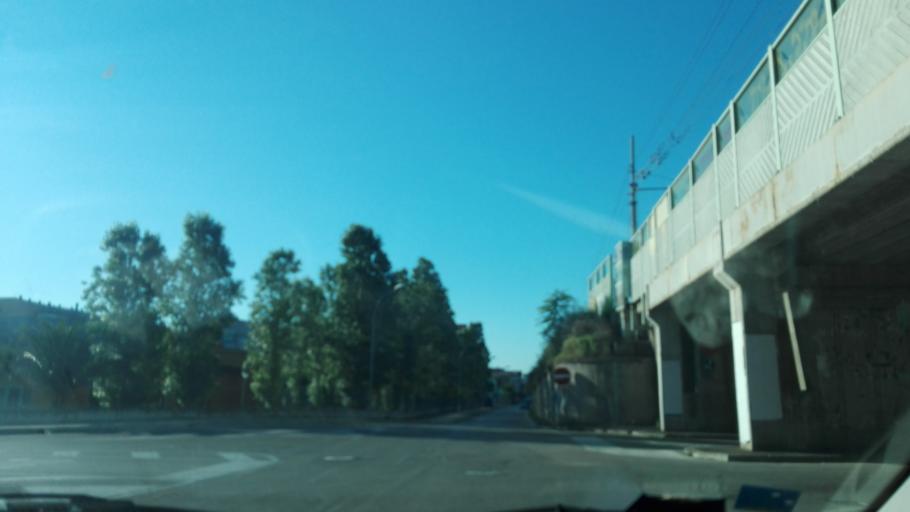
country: IT
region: Abruzzo
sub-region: Provincia di Pescara
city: Villa Raspa
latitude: 42.4840
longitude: 14.1872
